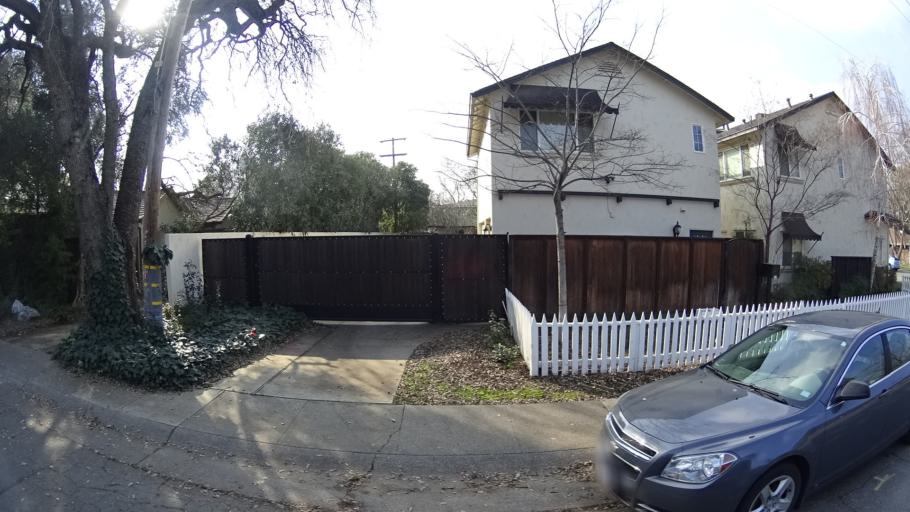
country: US
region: California
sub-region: Yolo County
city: Davis
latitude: 38.5534
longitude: -121.7410
